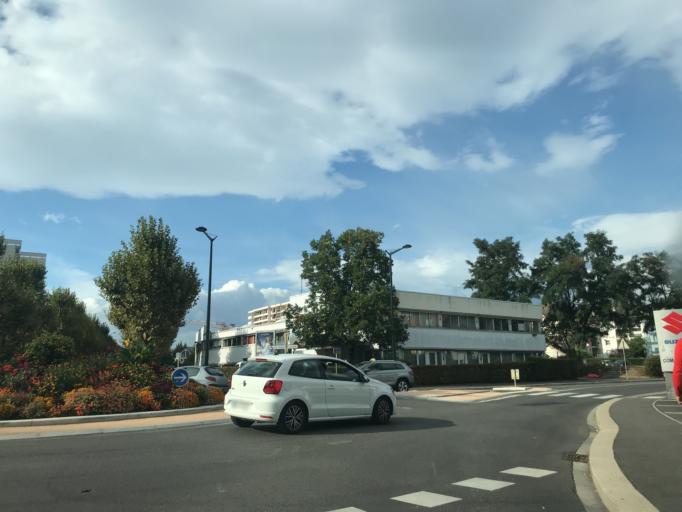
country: FR
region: Rhone-Alpes
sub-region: Departement de la Haute-Savoie
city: Annecy-le-Vieux
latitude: 45.9197
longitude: 6.1318
